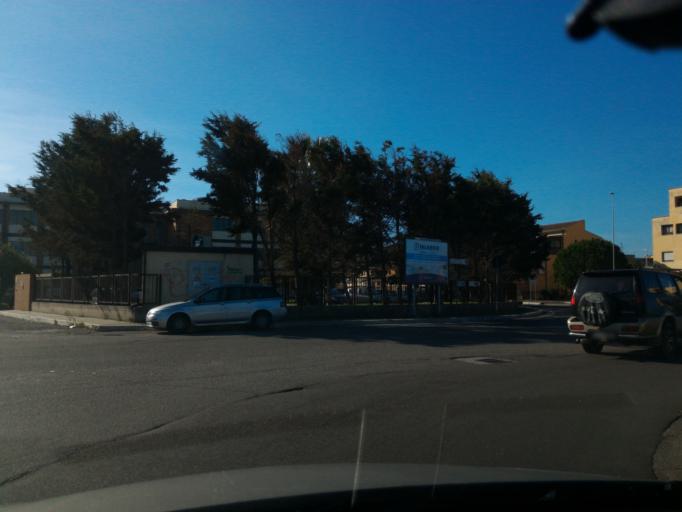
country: IT
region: Calabria
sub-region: Provincia di Crotone
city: Crotone
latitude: 39.0868
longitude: 17.1181
